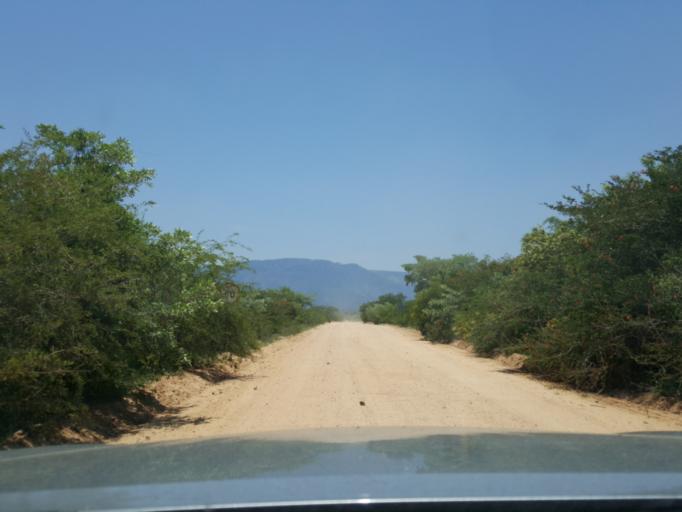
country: ZA
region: Limpopo
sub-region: Mopani District Municipality
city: Hoedspruit
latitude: -24.5680
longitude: 31.0053
